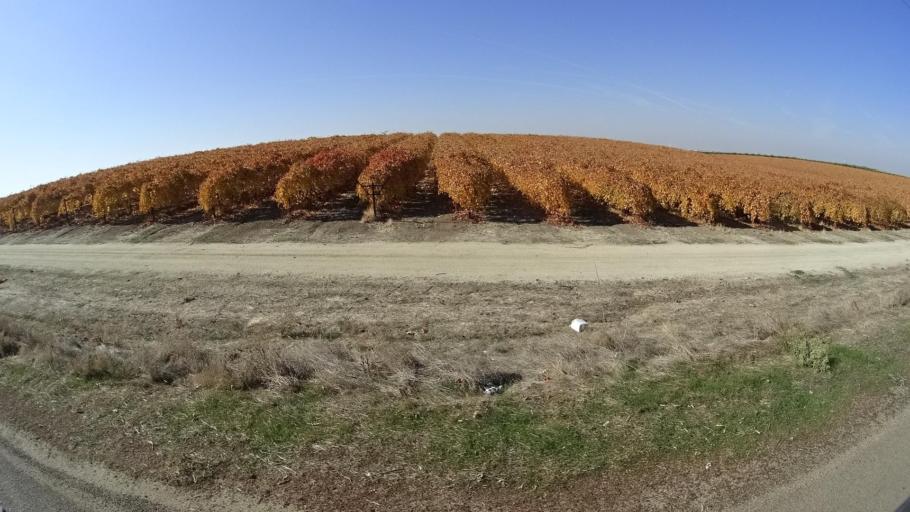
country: US
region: California
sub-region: Tulare County
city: Richgrove
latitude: 35.7081
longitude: -119.1338
